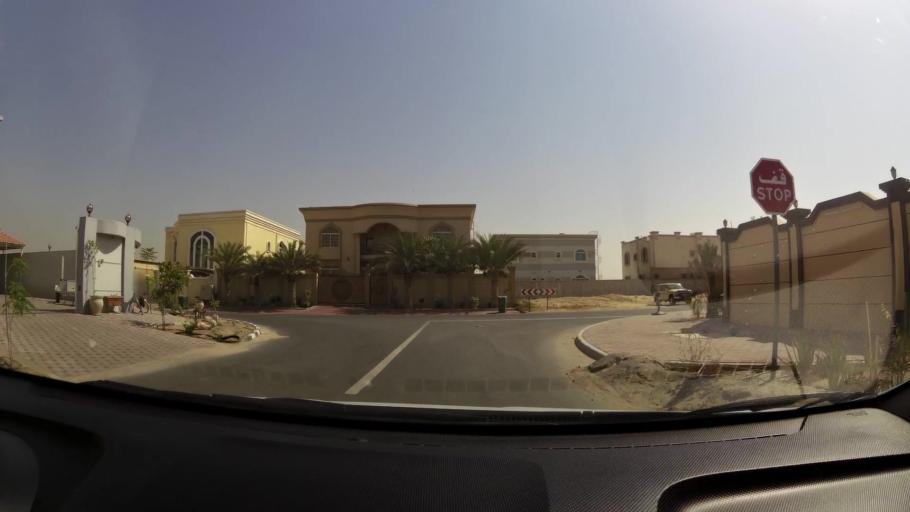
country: AE
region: Ajman
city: Ajman
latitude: 25.4149
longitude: 55.5444
